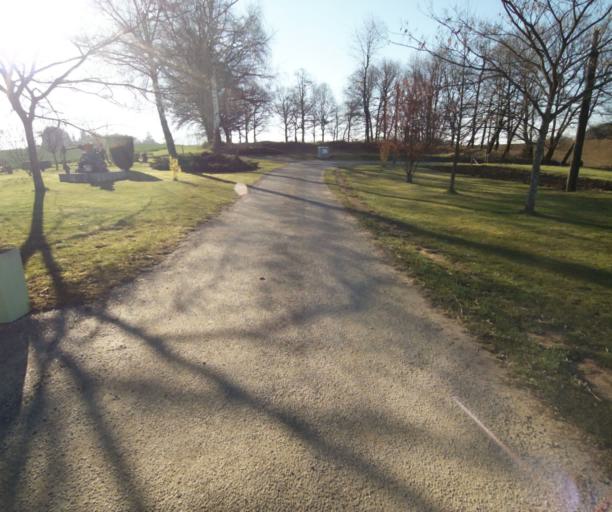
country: FR
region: Limousin
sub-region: Departement de la Correze
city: Uzerche
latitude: 45.3890
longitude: 1.6152
